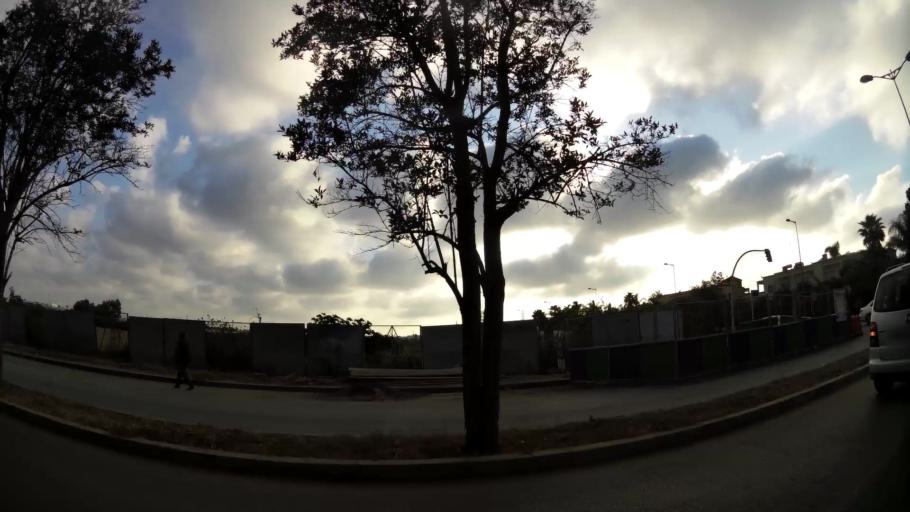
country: MA
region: Rabat-Sale-Zemmour-Zaer
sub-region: Rabat
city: Rabat
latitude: 33.9574
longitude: -6.8505
